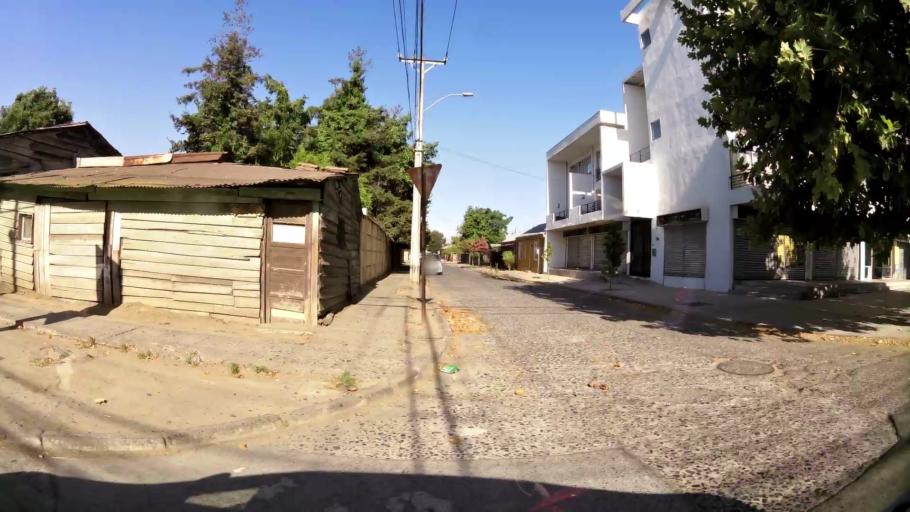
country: CL
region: Maule
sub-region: Provincia de Talca
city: Talca
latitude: -35.4385
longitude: -71.6660
